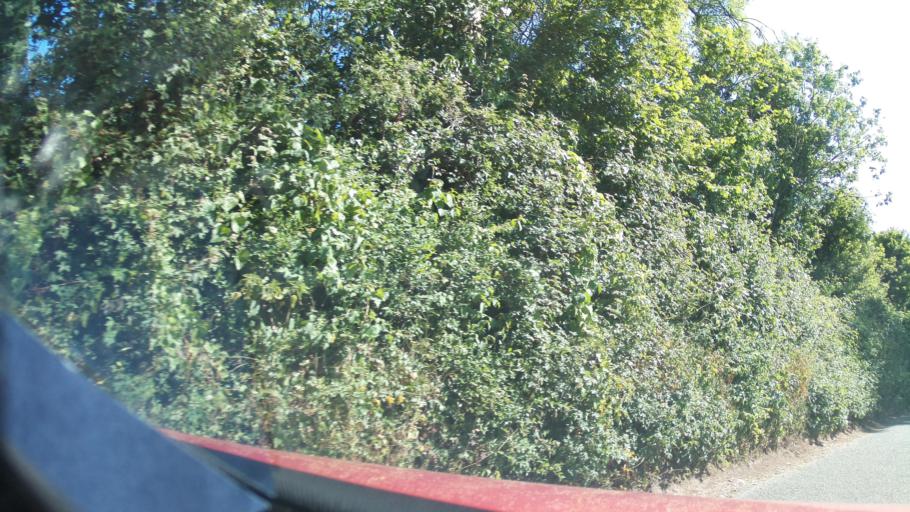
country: GB
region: England
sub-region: Devon
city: Marldon
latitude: 50.4144
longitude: -3.6112
